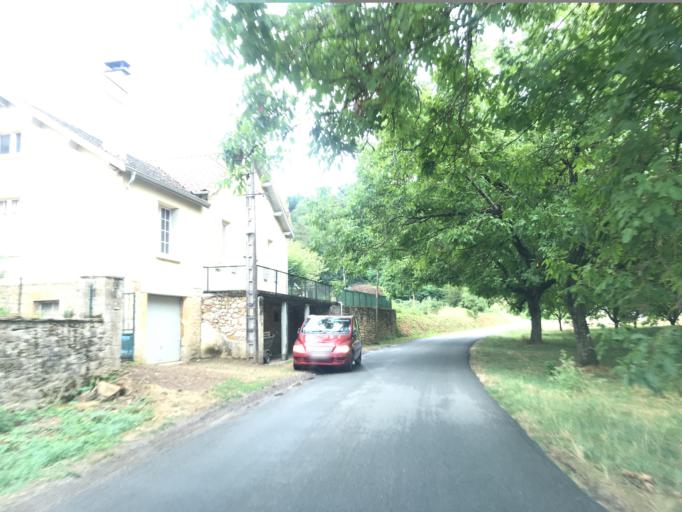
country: FR
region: Aquitaine
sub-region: Departement de la Dordogne
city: Domme
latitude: 44.8082
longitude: 1.2250
